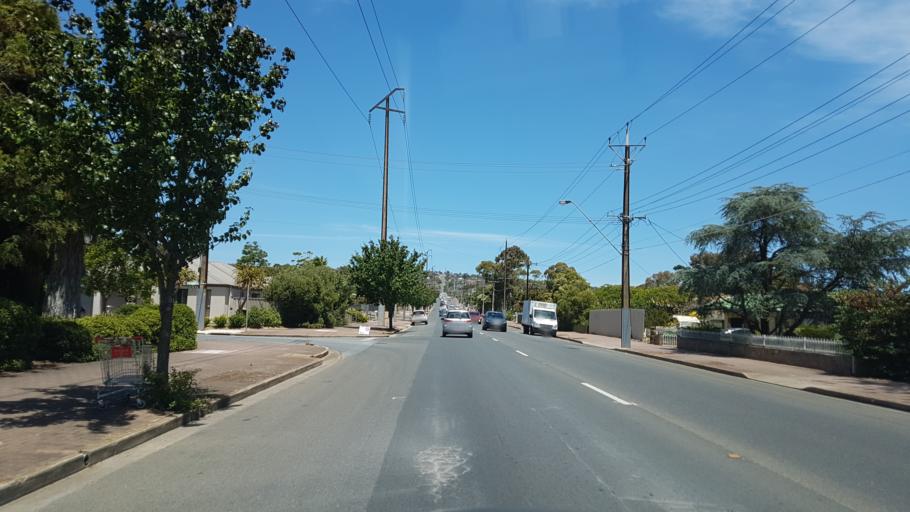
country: AU
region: South Australia
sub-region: Marion
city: Sturt
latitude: -35.0229
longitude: 138.5413
